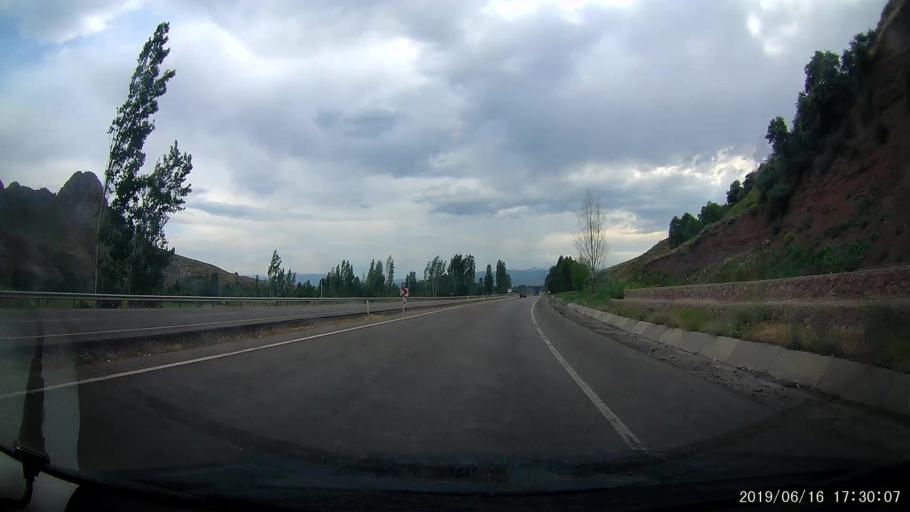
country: TR
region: Erzincan
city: Tercan
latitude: 39.7782
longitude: 40.3537
